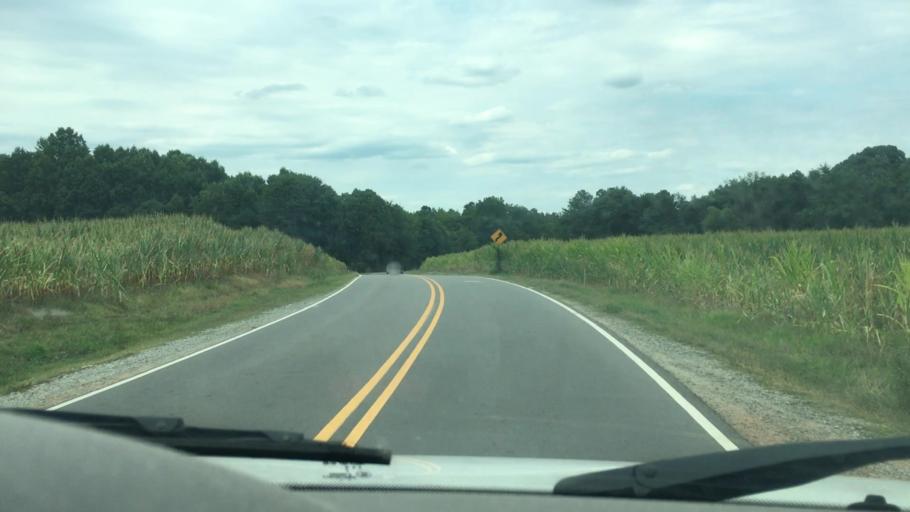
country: US
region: North Carolina
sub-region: Gaston County
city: Davidson
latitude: 35.4558
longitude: -80.8022
